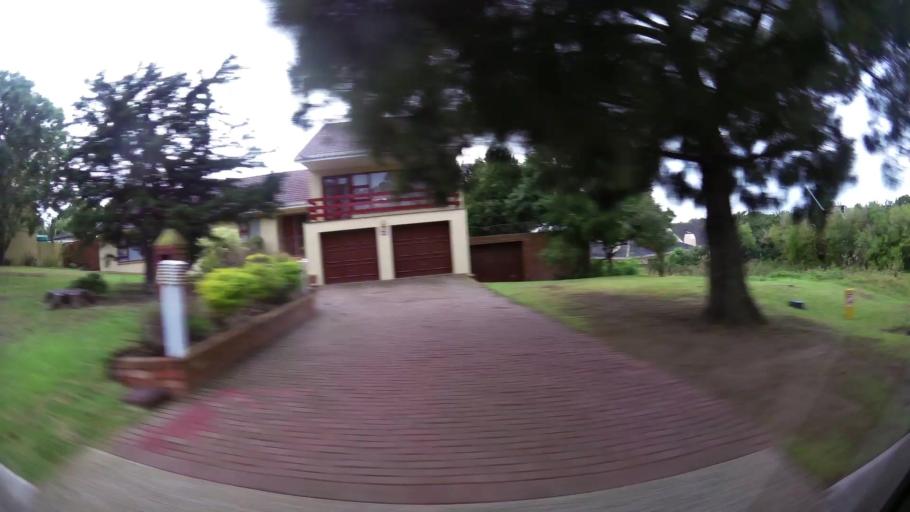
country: ZA
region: Eastern Cape
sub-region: Nelson Mandela Bay Metropolitan Municipality
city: Port Elizabeth
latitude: -33.9966
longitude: 25.5626
